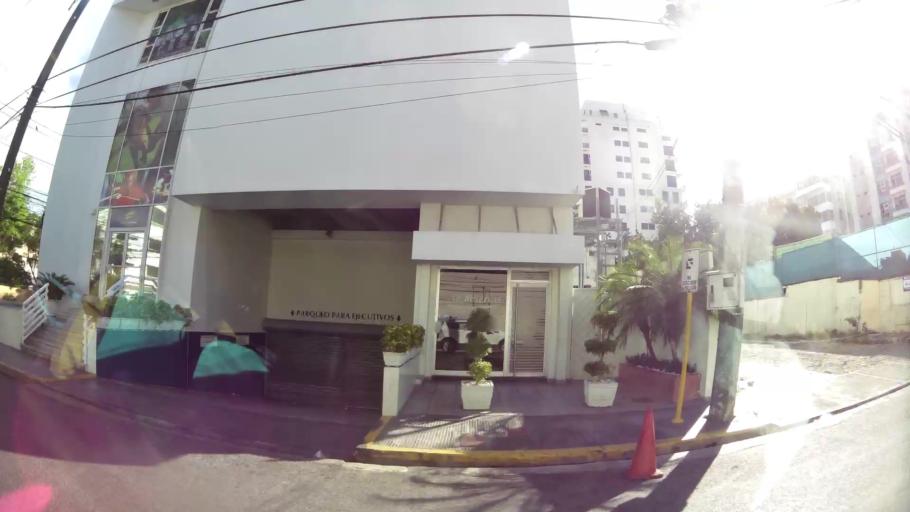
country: DO
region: Nacional
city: La Julia
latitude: 18.4728
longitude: -69.9393
